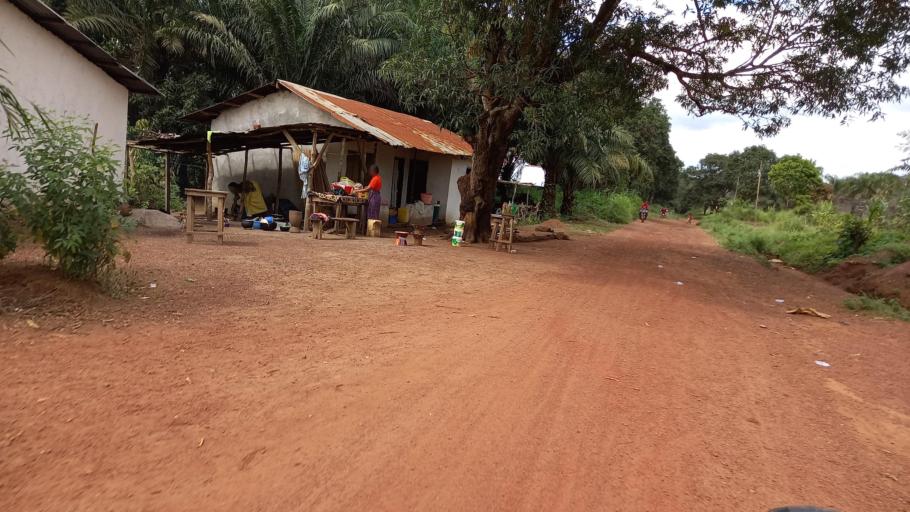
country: SL
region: Northern Province
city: Kamakwie
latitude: 9.5018
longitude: -12.2369
